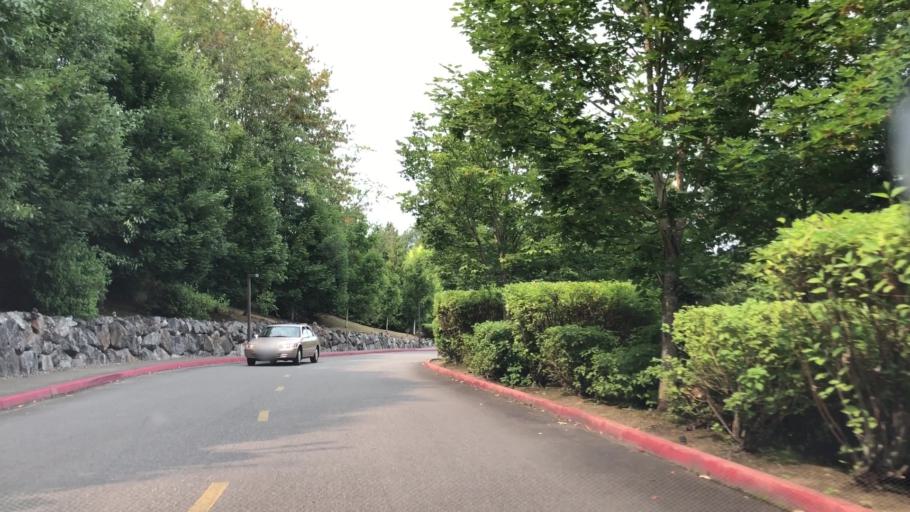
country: US
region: Washington
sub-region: King County
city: Bothell
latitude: 47.7551
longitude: -122.2032
